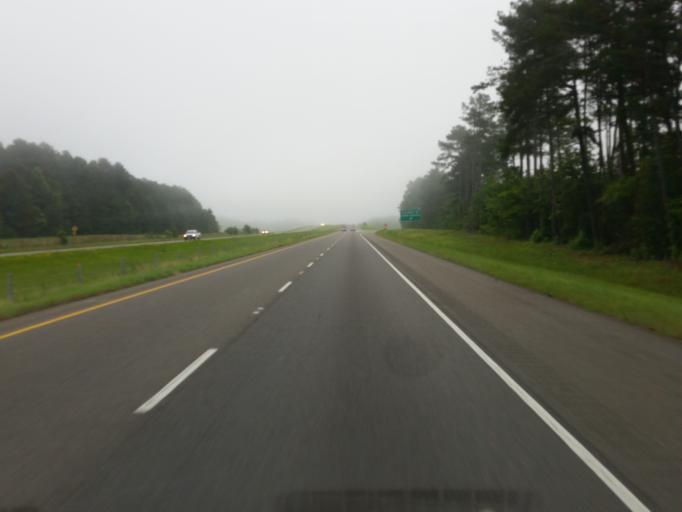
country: US
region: Louisiana
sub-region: Bossier Parish
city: Haughton
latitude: 32.5780
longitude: -93.4402
